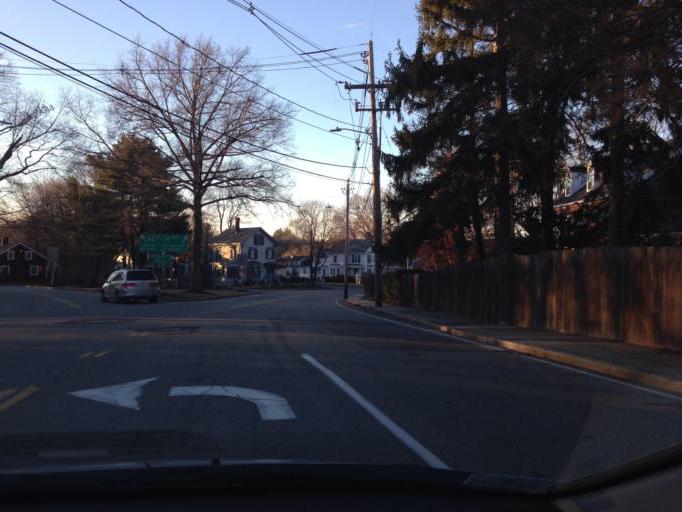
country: US
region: Massachusetts
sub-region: Middlesex County
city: Bedford
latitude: 42.4935
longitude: -71.2839
